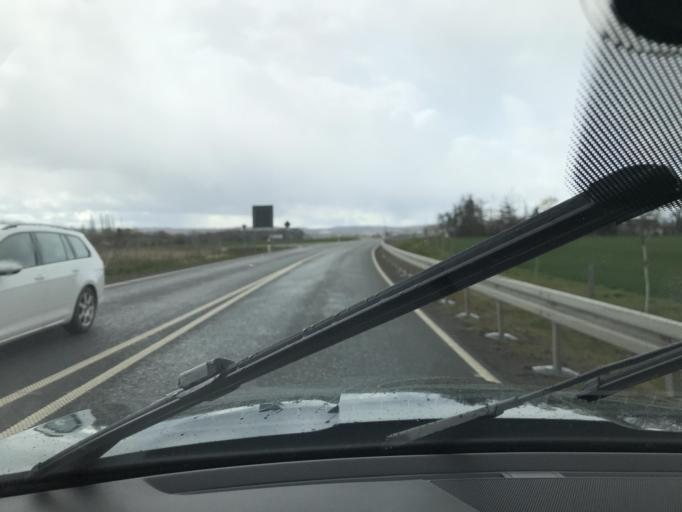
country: DE
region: Saxony-Anhalt
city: Ballenstedt
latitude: 51.7348
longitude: 11.2676
